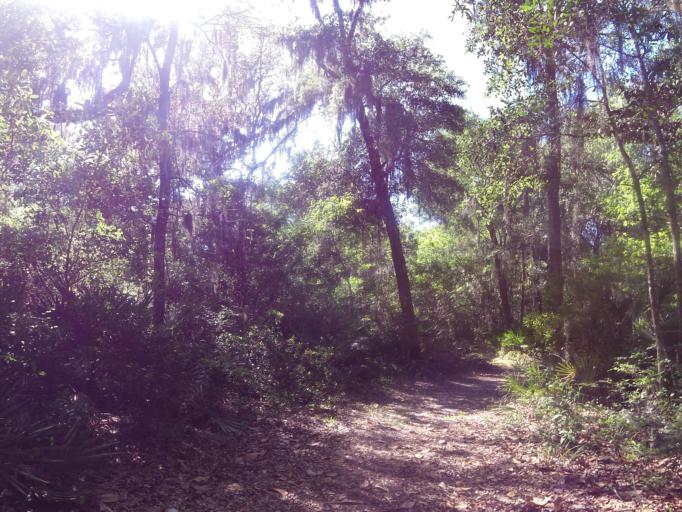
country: US
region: Florida
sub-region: Duval County
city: Atlantic Beach
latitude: 30.4563
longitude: -81.4802
